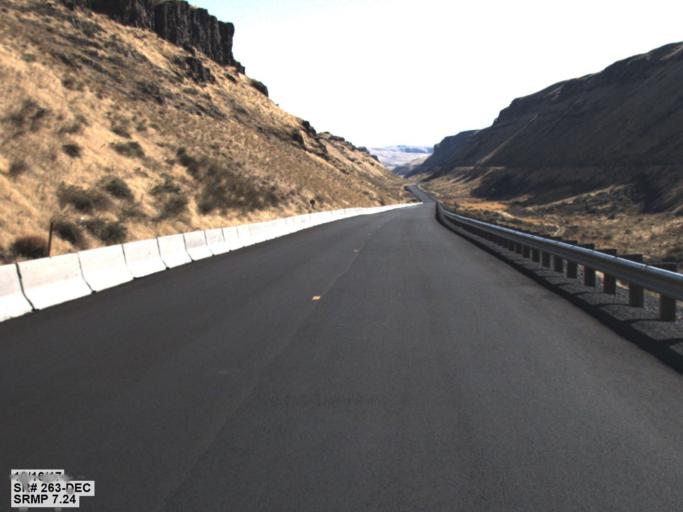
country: US
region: Washington
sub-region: Franklin County
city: Connell
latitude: 46.6186
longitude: -118.5575
